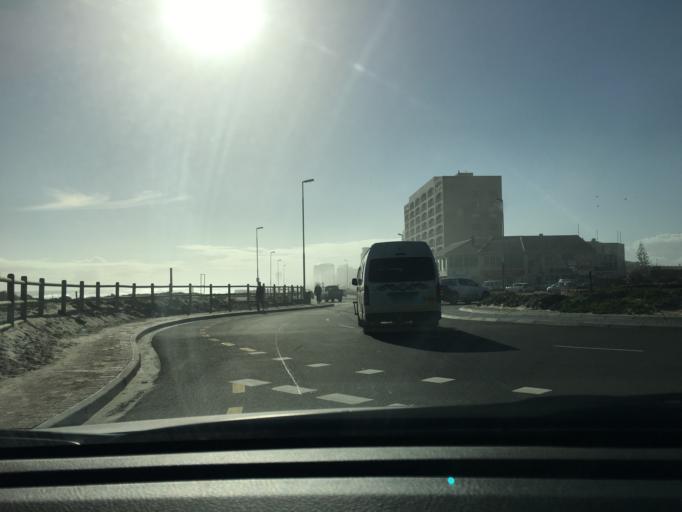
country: ZA
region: Western Cape
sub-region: City of Cape Town
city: Sunset Beach
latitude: -33.8218
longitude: 18.4766
